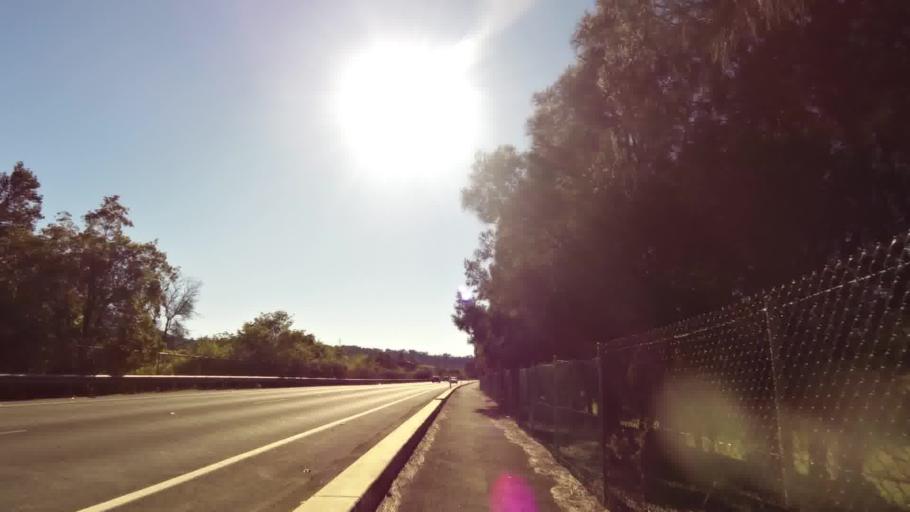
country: AU
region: New South Wales
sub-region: Wollongong
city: Koonawarra
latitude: -34.4790
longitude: 150.8060
